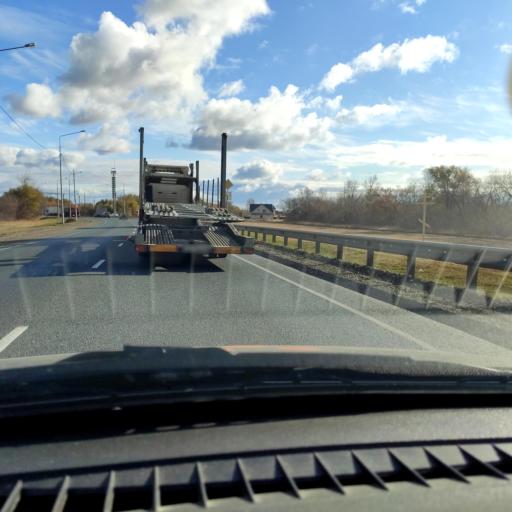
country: RU
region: Samara
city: Varlamovo
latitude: 53.1909
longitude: 48.3516
